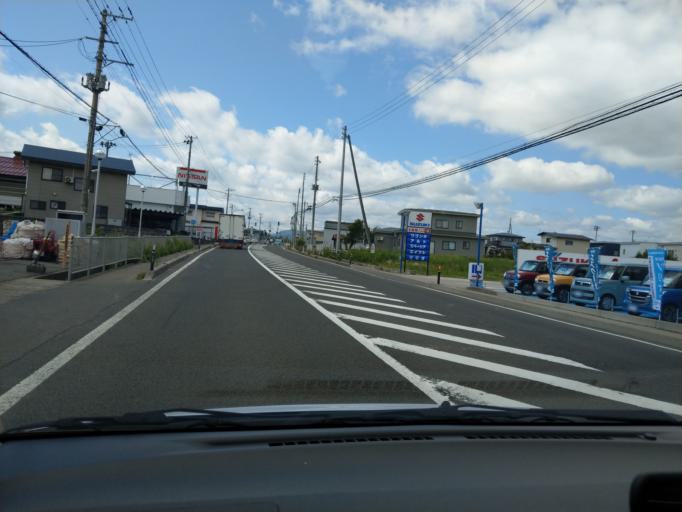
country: JP
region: Akita
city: Yuzawa
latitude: 39.1894
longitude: 140.5015
